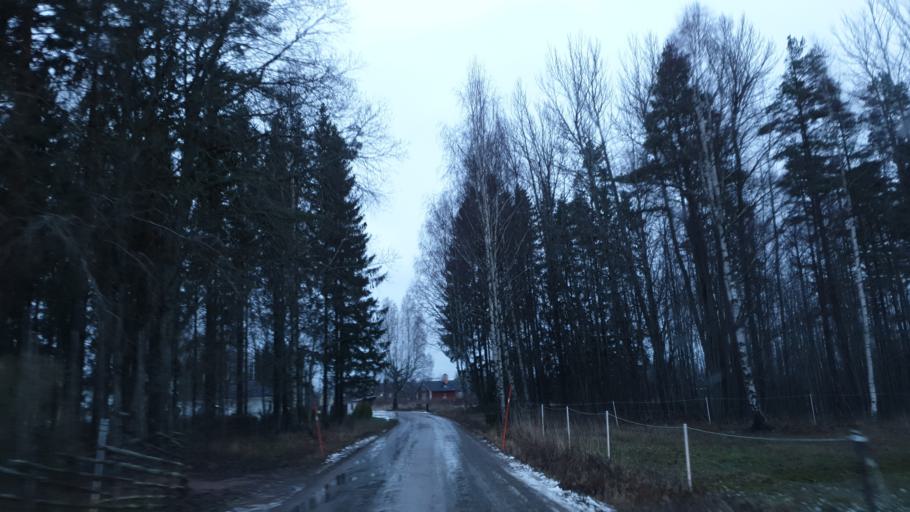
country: SE
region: Uppsala
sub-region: Tierps Kommun
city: Tierp
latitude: 60.3406
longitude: 17.4747
